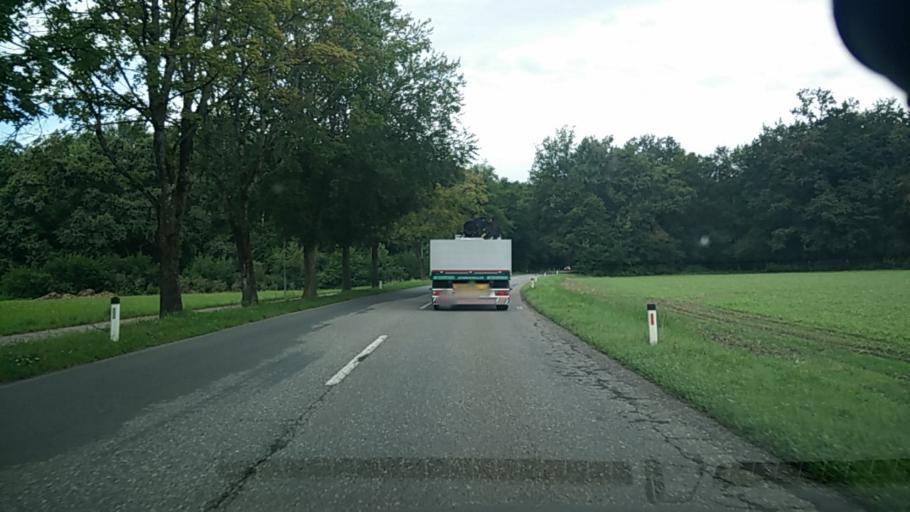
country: AT
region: Carinthia
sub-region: Klagenfurt am Woerthersee
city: Klagenfurt am Woerthersee
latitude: 46.6083
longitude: 14.2643
